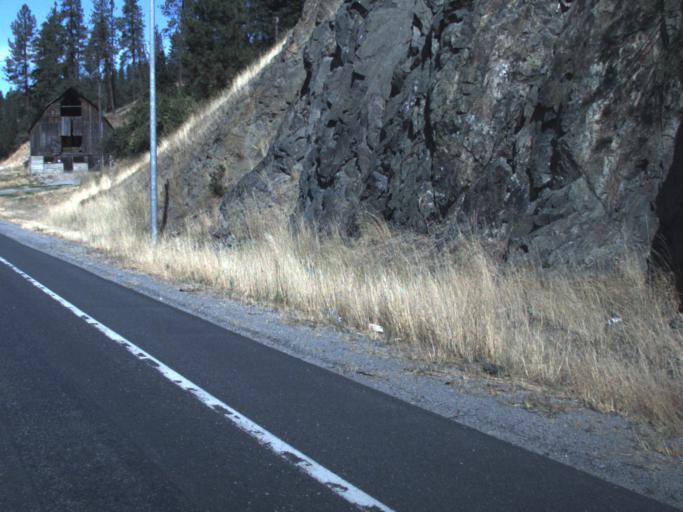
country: US
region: Washington
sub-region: Stevens County
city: Chewelah
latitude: 48.3193
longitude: -117.8181
